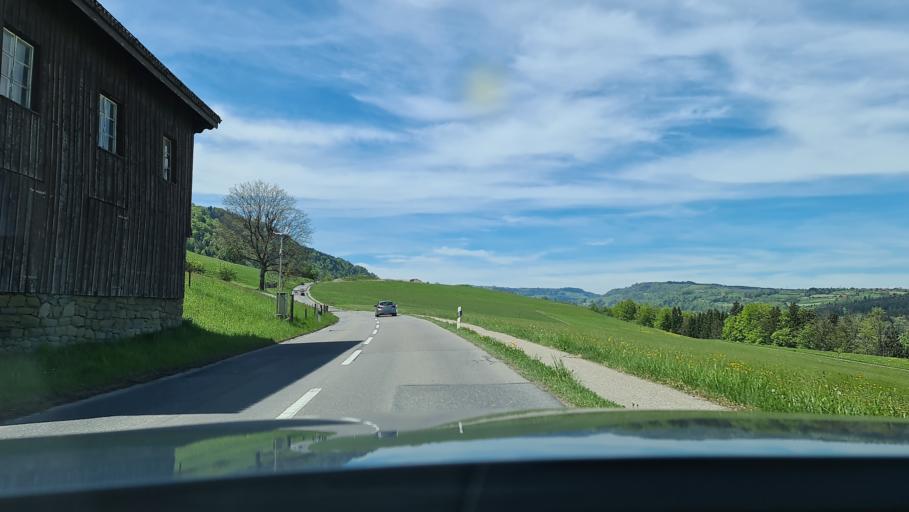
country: CH
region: Lucerne
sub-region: Lucerne-Stadt District
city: Littau
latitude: 47.0454
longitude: 8.2526
